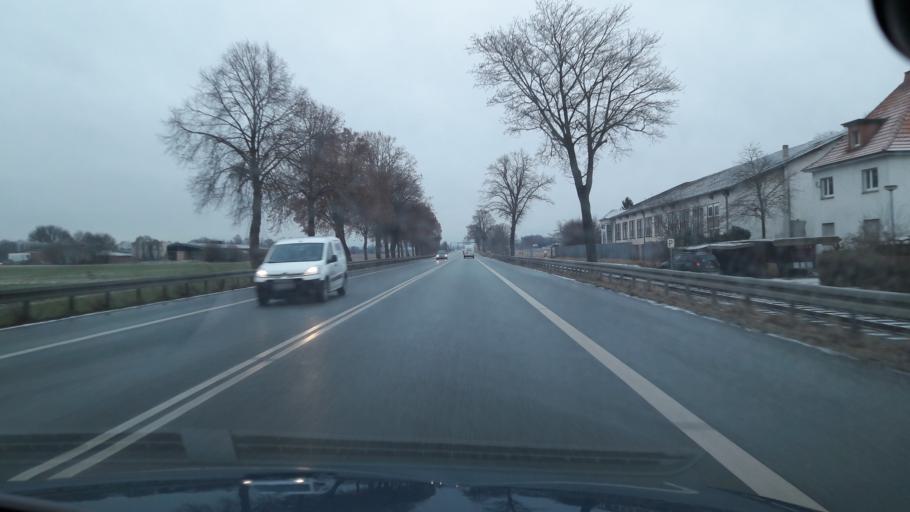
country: DE
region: North Rhine-Westphalia
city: Erwitte
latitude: 51.6386
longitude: 8.3421
